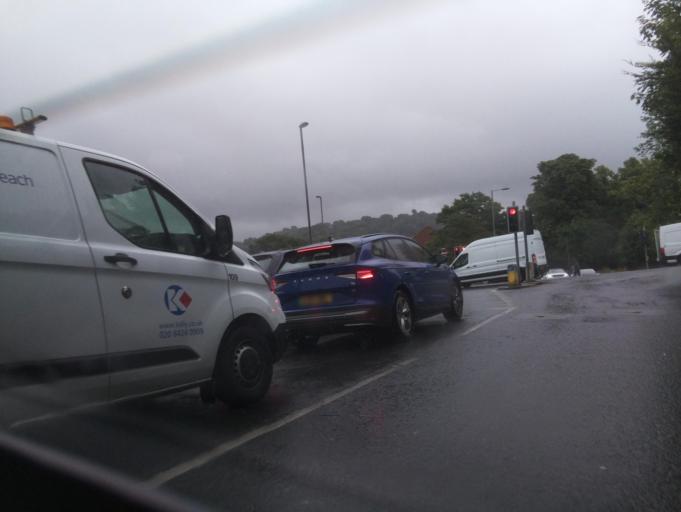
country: GB
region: England
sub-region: Surrey
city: Redhill
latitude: 51.2325
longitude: -0.1728
